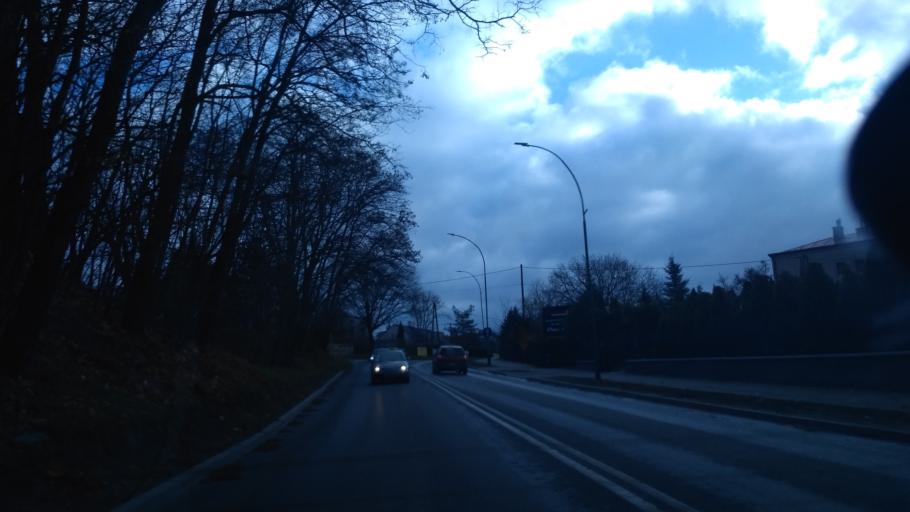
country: PL
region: Subcarpathian Voivodeship
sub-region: Powiat lancucki
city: Lancut
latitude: 50.0770
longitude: 22.2354
